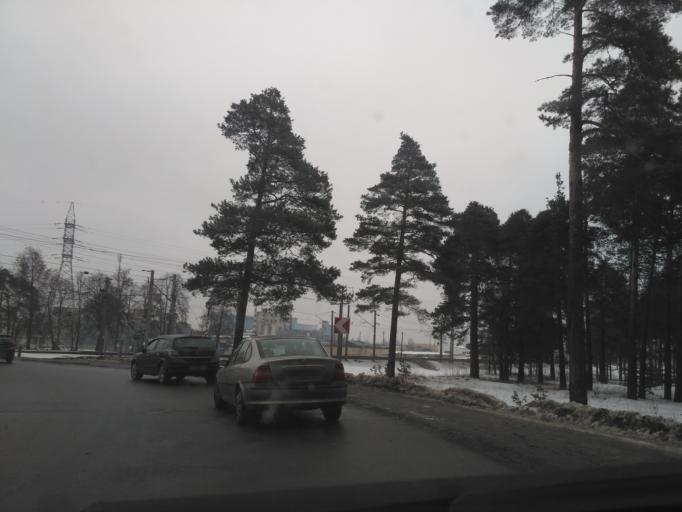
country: BY
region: Minsk
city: Horad Barysaw
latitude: 54.1964
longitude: 28.5153
